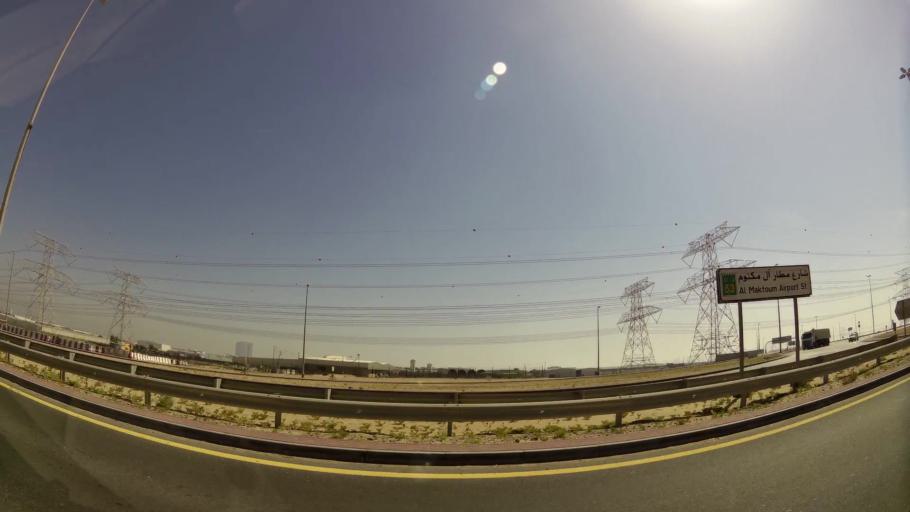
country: AE
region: Dubai
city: Dubai
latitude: 24.9373
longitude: 55.0754
